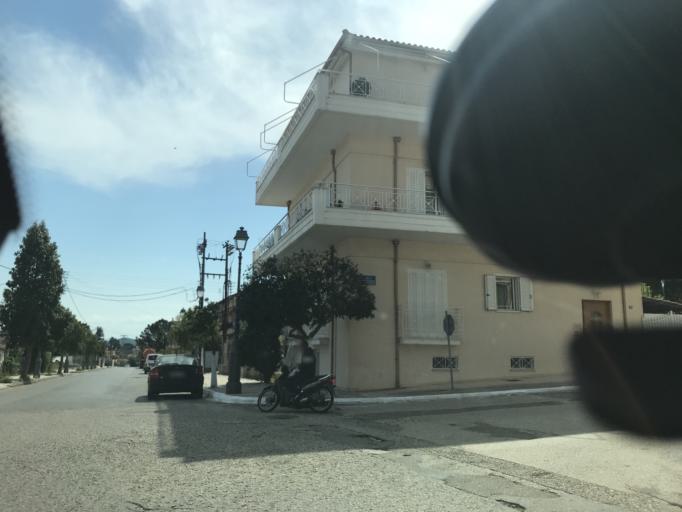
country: GR
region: West Greece
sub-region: Nomos Ileias
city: Pyrgos
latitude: 37.6744
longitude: 21.4468
